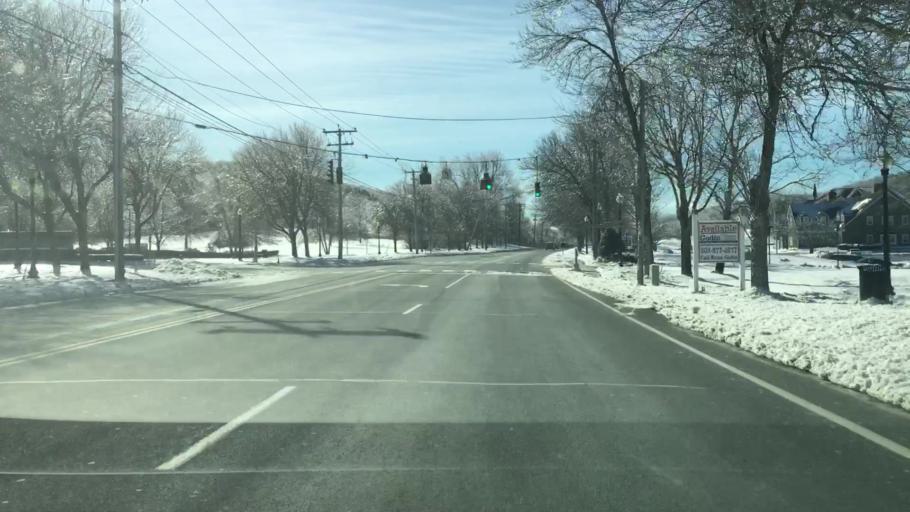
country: US
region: Connecticut
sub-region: New Haven County
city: Heritage Village
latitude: 41.4626
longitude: -73.2326
